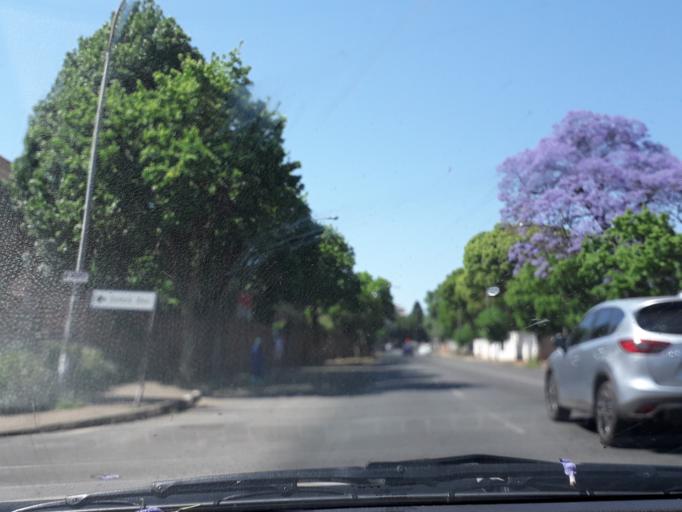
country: ZA
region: Gauteng
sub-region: City of Johannesburg Metropolitan Municipality
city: Johannesburg
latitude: -26.1621
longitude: 28.0476
